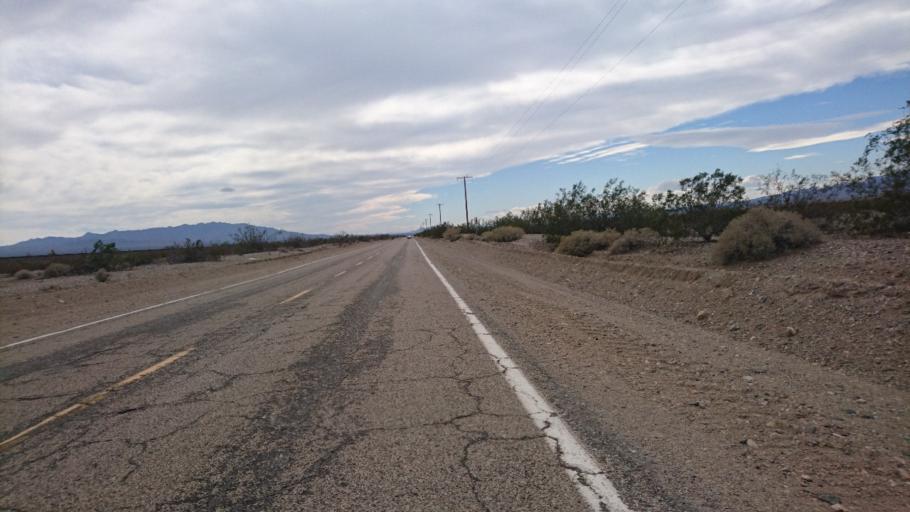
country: US
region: California
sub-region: San Bernardino County
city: Needles
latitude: 34.7902
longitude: -115.2015
